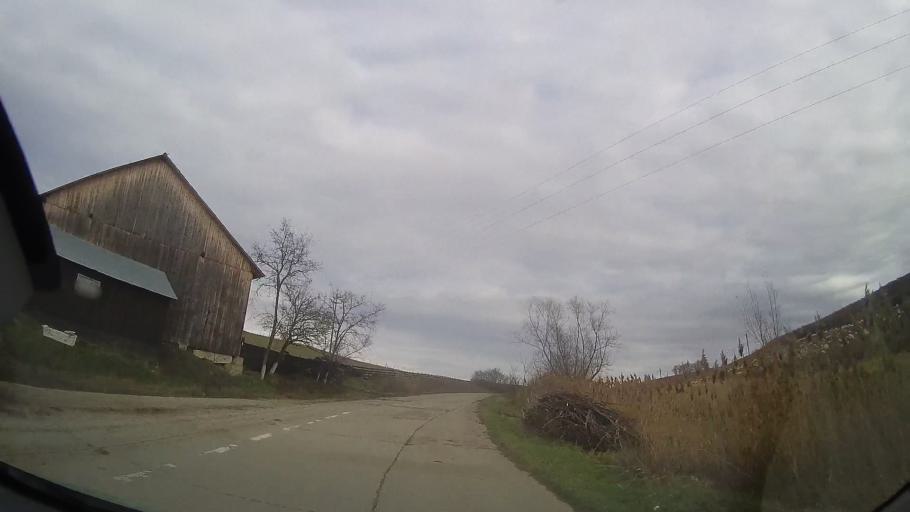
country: RO
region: Bistrita-Nasaud
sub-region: Comuna Micestii de Campie
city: Micestii de Campie
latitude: 46.8457
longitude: 24.3002
